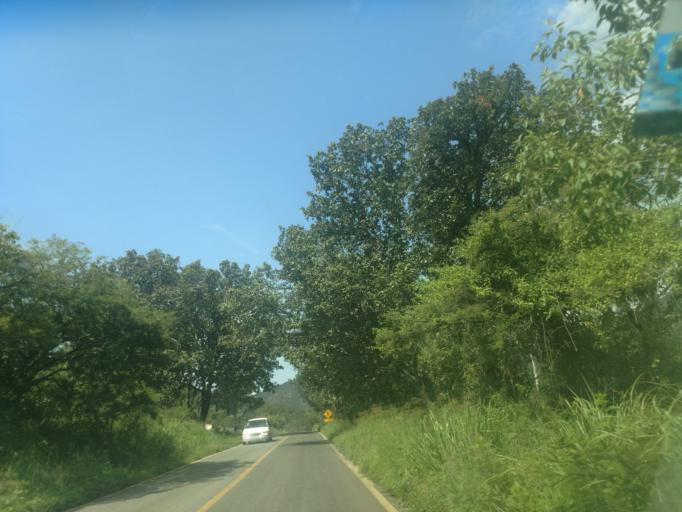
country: MX
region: Jalisco
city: Talpa de Allende
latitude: 20.4350
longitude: -104.7832
